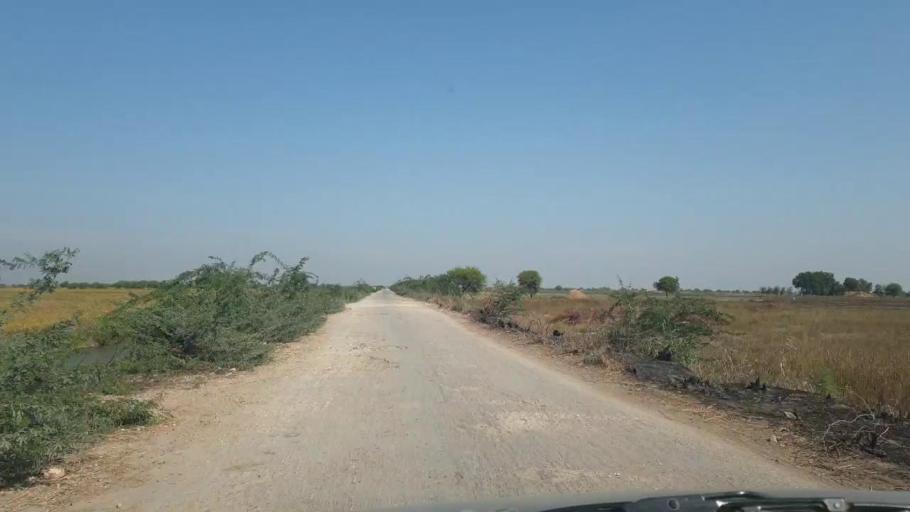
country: PK
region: Sindh
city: Tando Bago
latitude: 24.8226
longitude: 68.9861
